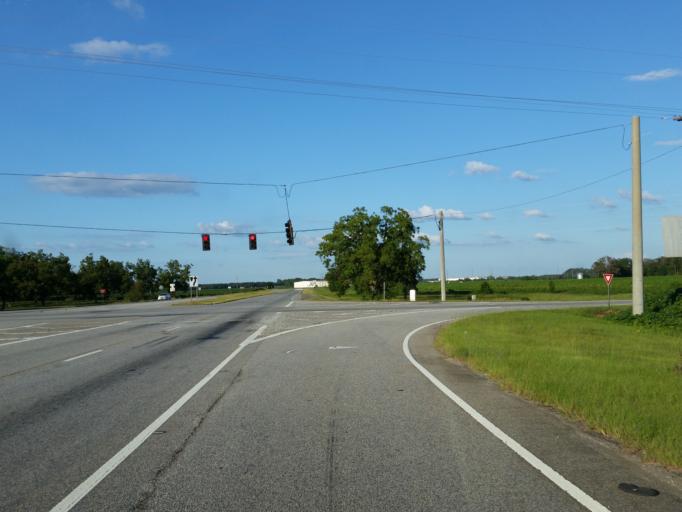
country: US
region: Georgia
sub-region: Houston County
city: Perry
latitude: 32.4828
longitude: -83.7701
